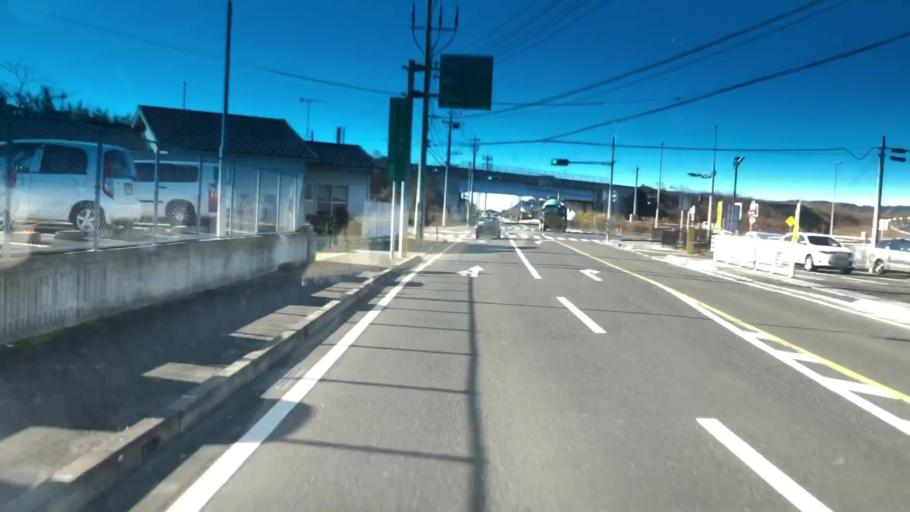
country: JP
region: Kagoshima
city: Satsumasendai
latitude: 31.8212
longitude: 130.2614
